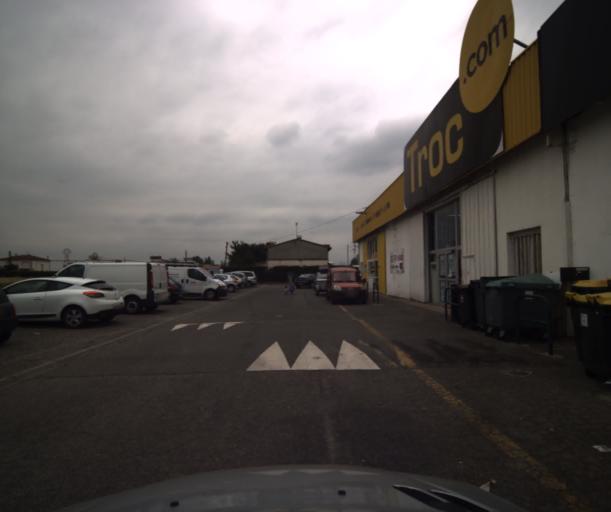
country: FR
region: Midi-Pyrenees
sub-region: Departement de la Haute-Garonne
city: Portet-sur-Garonne
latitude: 43.5367
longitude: 1.3985
